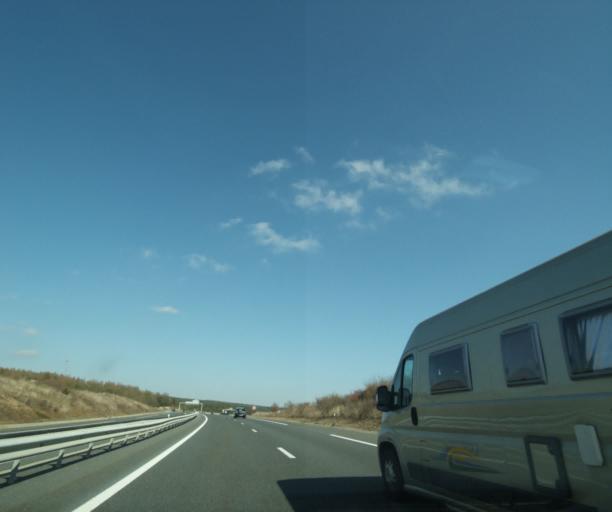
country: FR
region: Midi-Pyrenees
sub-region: Departement de l'Aveyron
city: Millau
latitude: 44.1692
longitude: 3.0310
